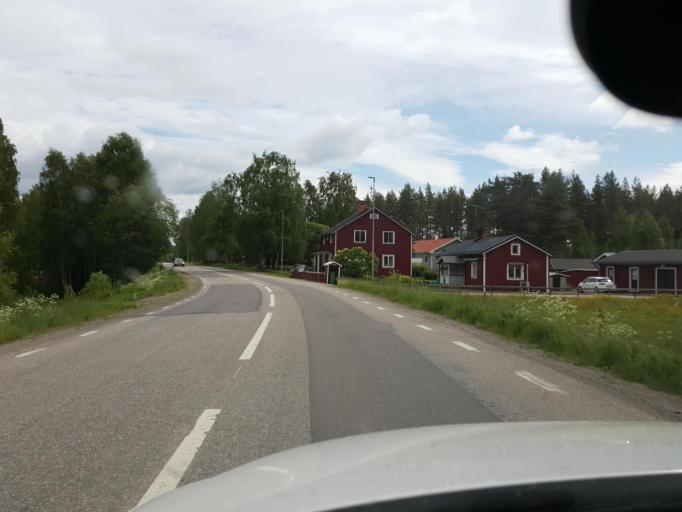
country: SE
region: Gaevleborg
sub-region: Ljusdals Kommun
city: Farila
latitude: 61.8097
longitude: 15.7603
